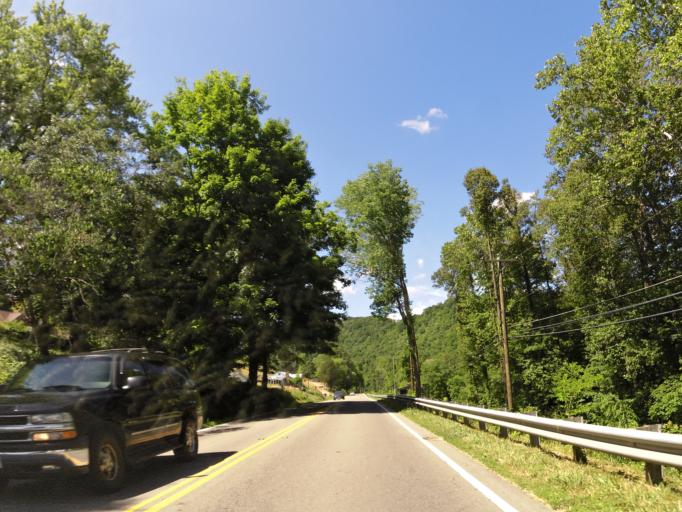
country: US
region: Virginia
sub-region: Lee County
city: Pennington Gap
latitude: 36.7381
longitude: -83.0005
